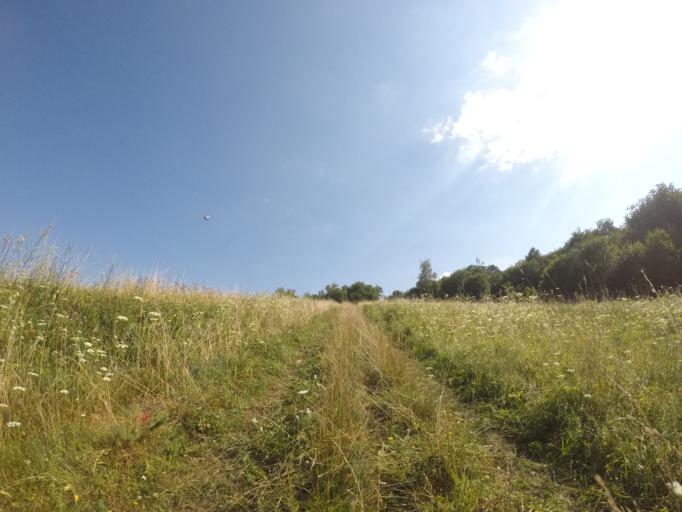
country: SK
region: Presovsky
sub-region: Okres Presov
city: Presov
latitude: 48.9397
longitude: 21.1671
